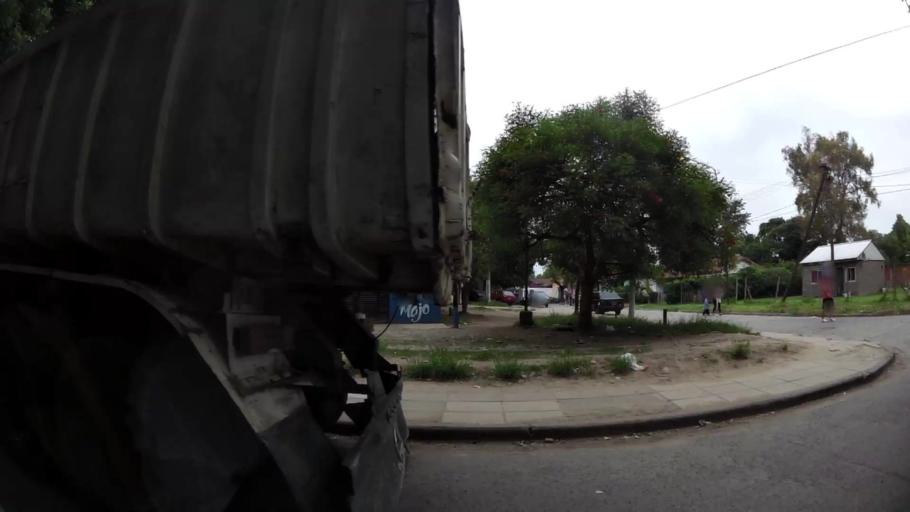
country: AR
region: Buenos Aires
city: San Justo
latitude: -34.7043
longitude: -58.5404
